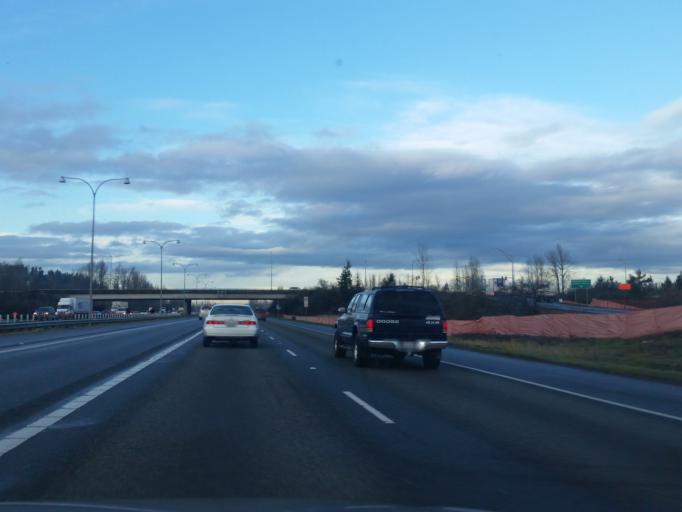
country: US
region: Washington
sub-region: King County
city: Auburn
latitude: 47.3202
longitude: -122.2448
